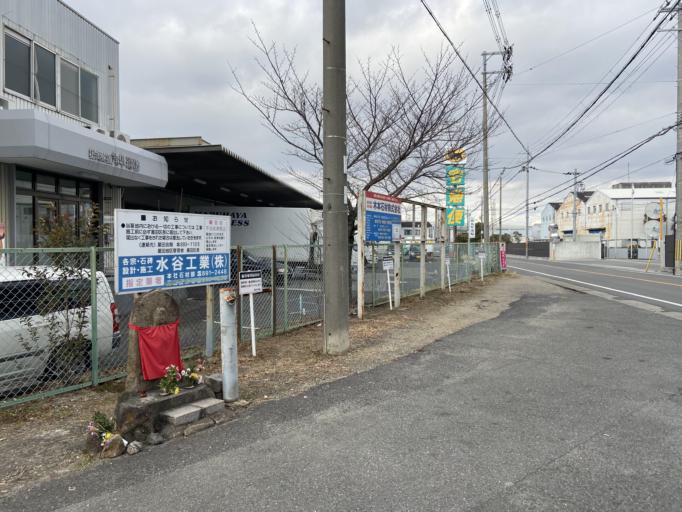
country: JP
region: Osaka
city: Hirakata
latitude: 34.7756
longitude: 135.6696
